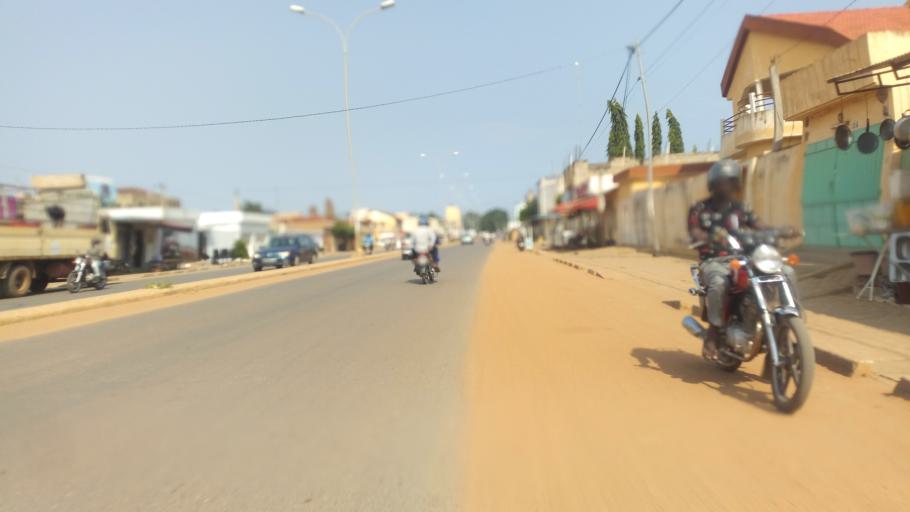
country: TG
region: Maritime
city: Lome
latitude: 6.1983
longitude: 1.1843
